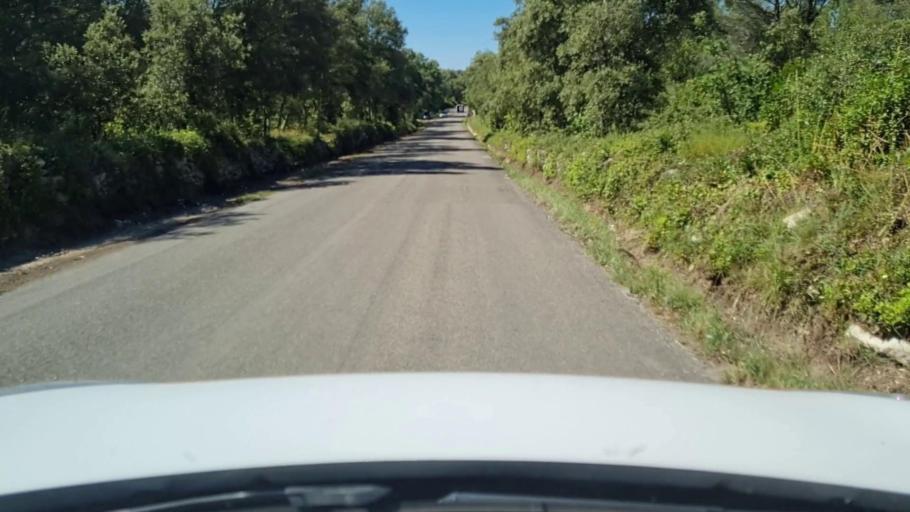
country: FR
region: Languedoc-Roussillon
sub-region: Departement du Gard
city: Villevieille
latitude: 43.7833
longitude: 4.1200
